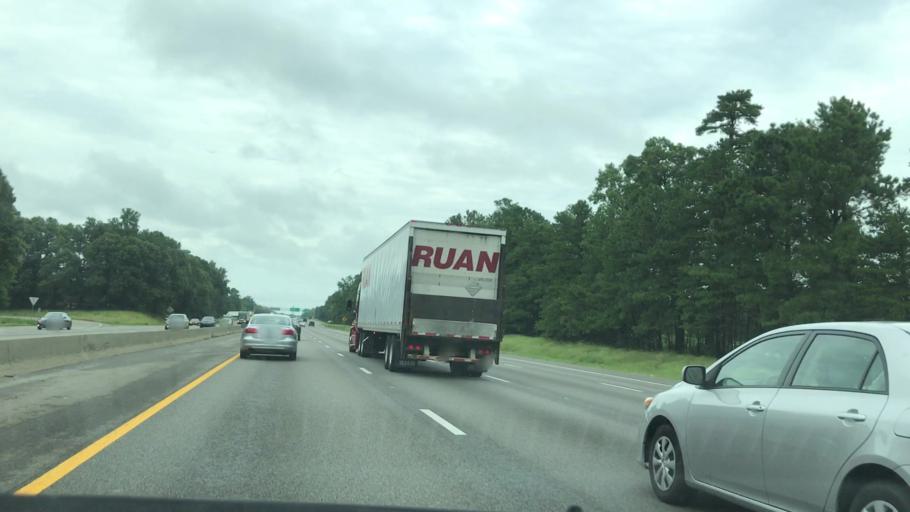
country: US
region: Virginia
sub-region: Chesterfield County
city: Chester
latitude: 37.3483
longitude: -77.4053
